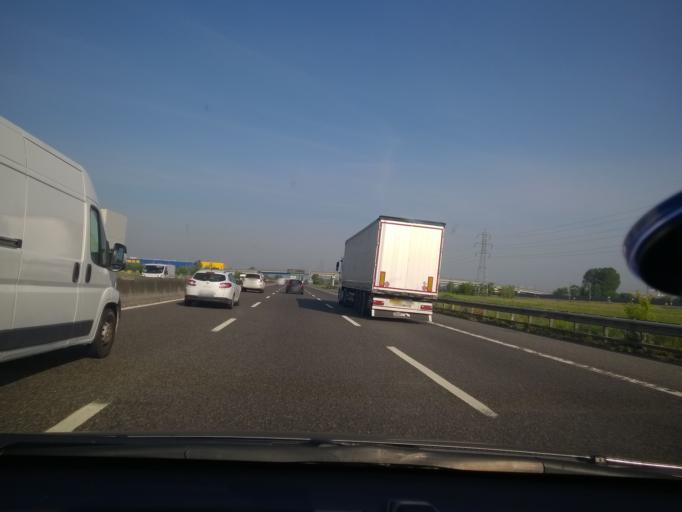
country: IT
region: Emilia-Romagna
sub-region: Provincia di Parma
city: Parma
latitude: 44.8294
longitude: 10.3719
